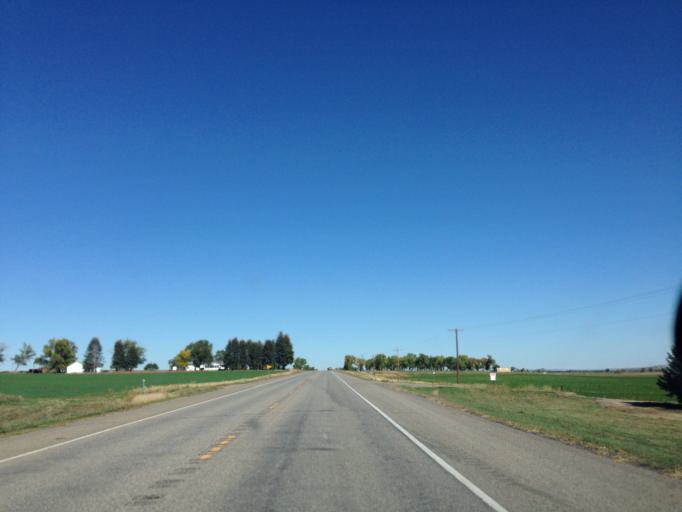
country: US
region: Montana
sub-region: Yellowstone County
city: Laurel
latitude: 45.4818
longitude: -108.8630
